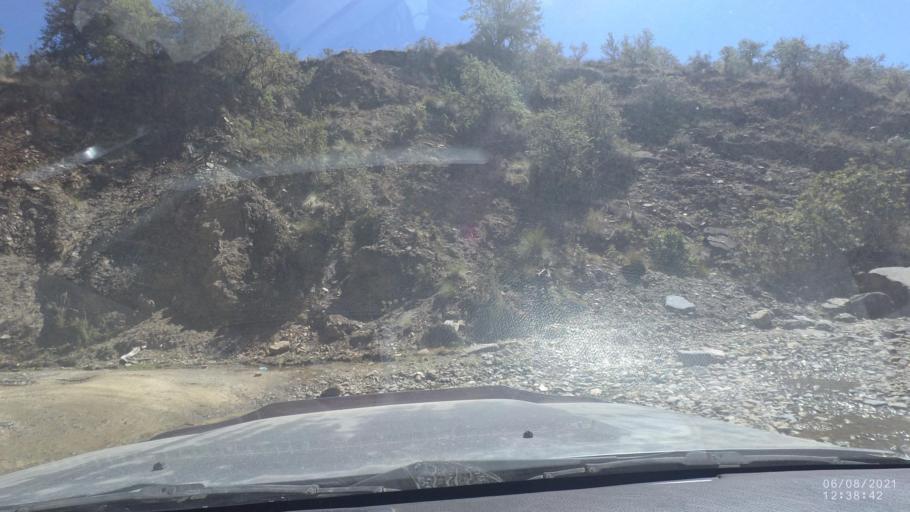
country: BO
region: Cochabamba
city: Colchani
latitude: -16.7763
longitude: -66.6619
